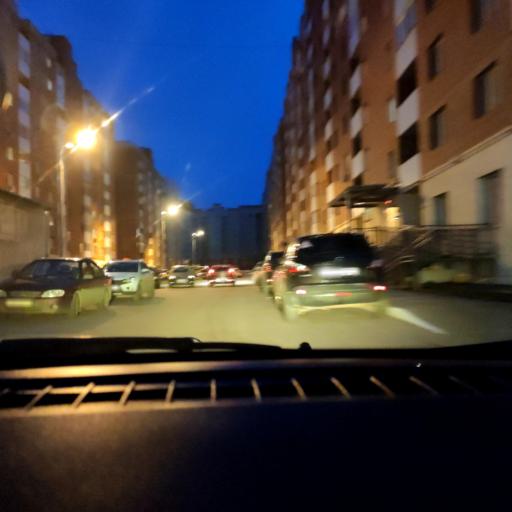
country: RU
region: Samara
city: Petra-Dubrava
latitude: 53.3079
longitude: 50.2857
